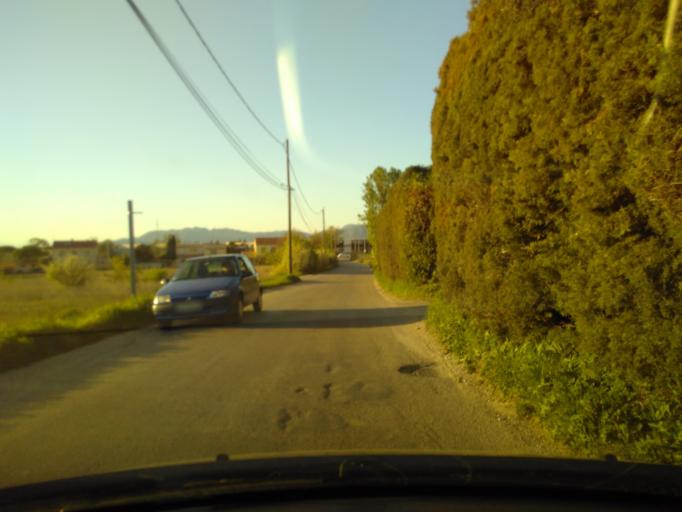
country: FR
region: Provence-Alpes-Cote d'Azur
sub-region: Departement du Vaucluse
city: Carpentras
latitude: 44.0570
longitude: 5.0701
